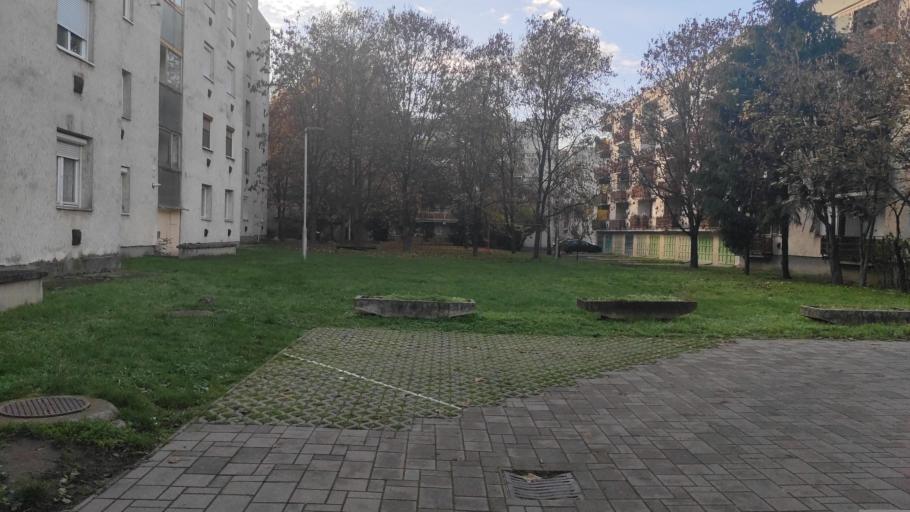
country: HU
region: Bekes
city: Bekes
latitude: 46.7709
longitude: 21.1288
